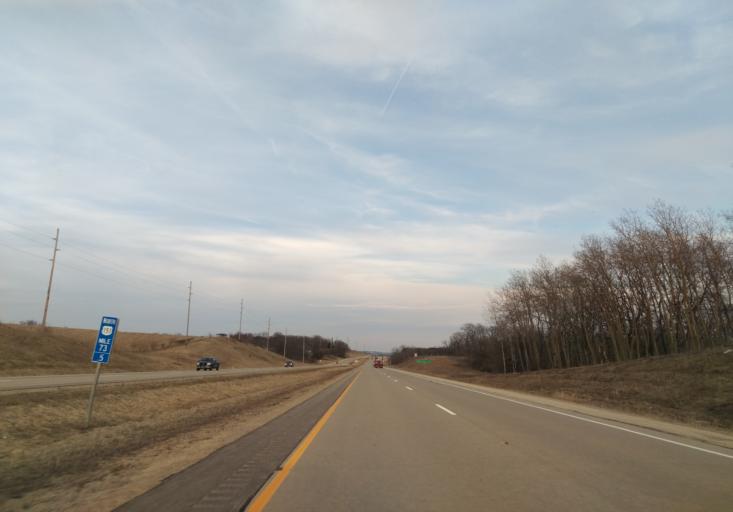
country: US
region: Wisconsin
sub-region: Dane County
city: Verona
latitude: 42.9882
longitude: -89.6241
